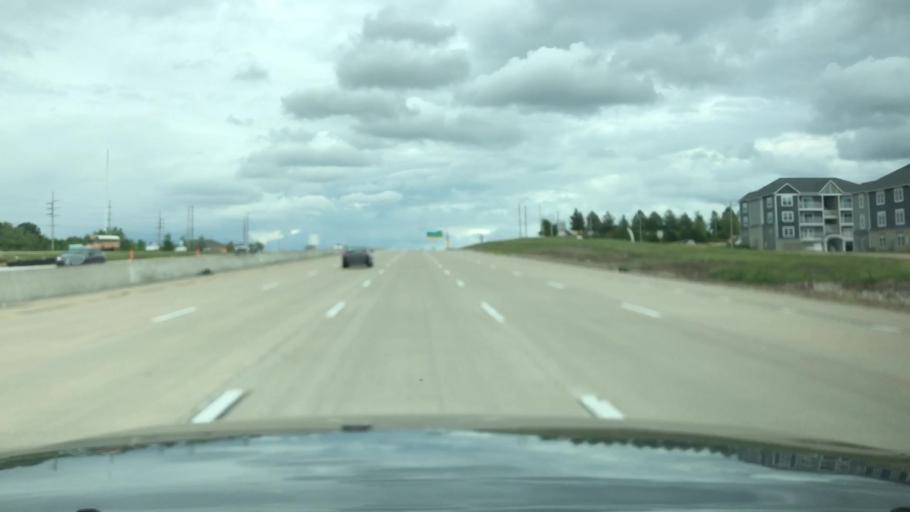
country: US
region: Missouri
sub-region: Saint Charles County
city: Cottleville
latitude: 38.7389
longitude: -90.6274
